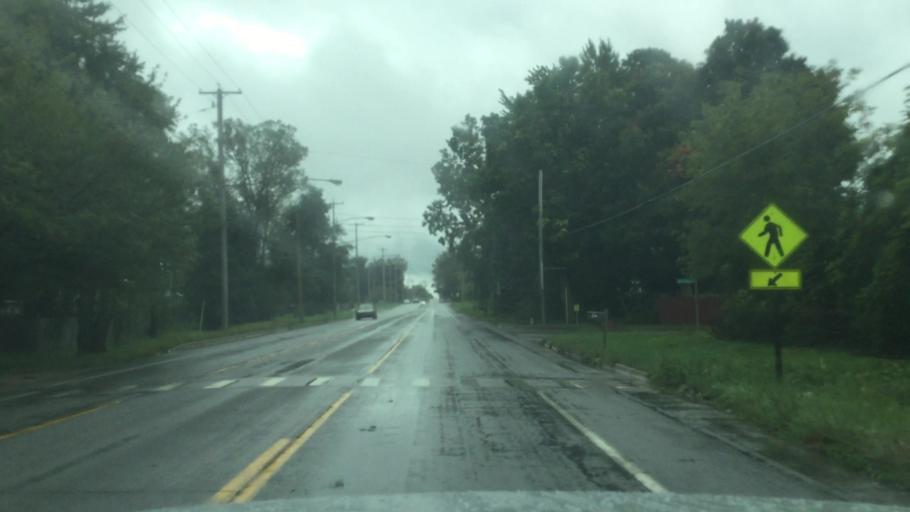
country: US
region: Michigan
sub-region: Eaton County
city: Dimondale
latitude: 42.6740
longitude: -84.6030
